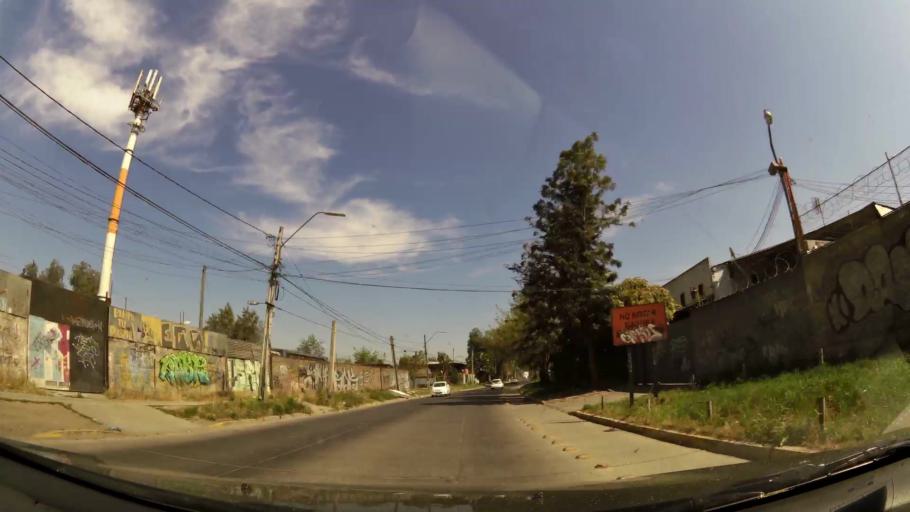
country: CL
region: Santiago Metropolitan
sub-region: Provincia de Santiago
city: Lo Prado
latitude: -33.4019
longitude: -70.7236
